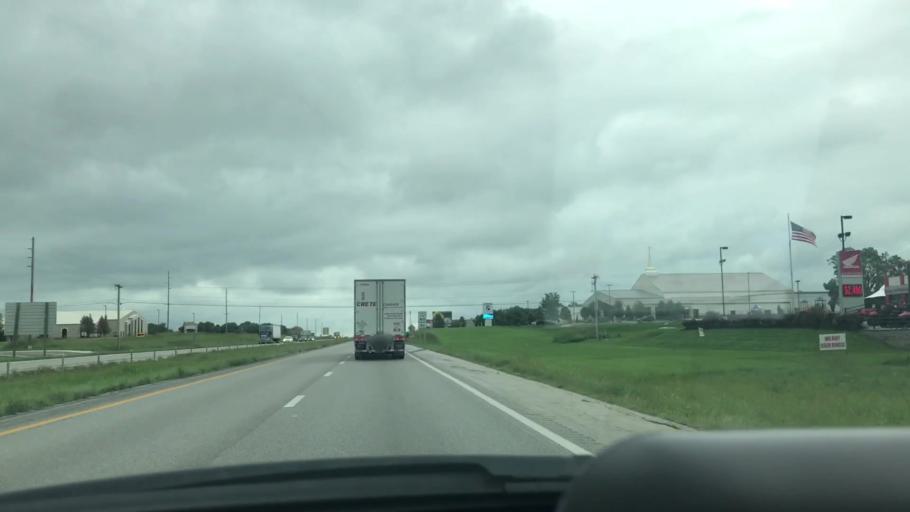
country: US
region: Missouri
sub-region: Greene County
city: Springfield
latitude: 37.2499
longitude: -93.2532
